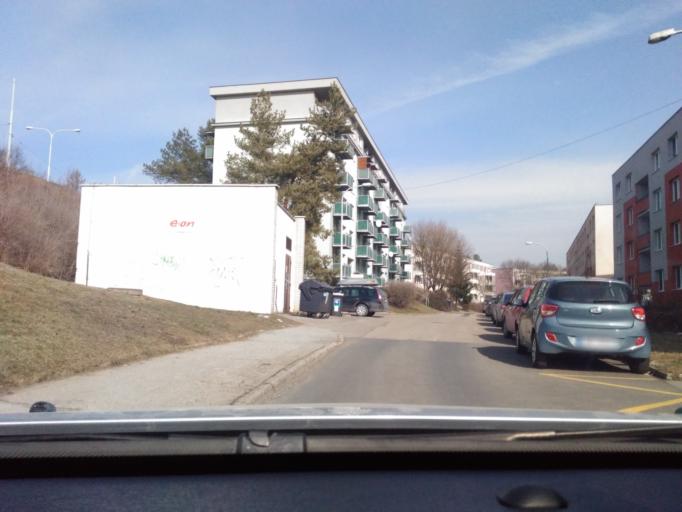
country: CZ
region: South Moravian
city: Troubsko
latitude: 49.2185
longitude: 16.5256
